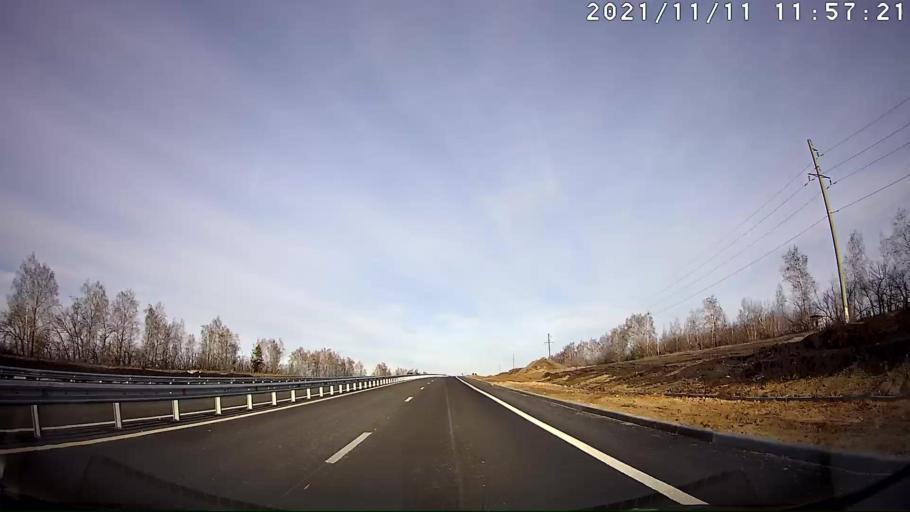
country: RU
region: Samara
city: Balasheyka
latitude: 53.5649
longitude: 48.3298
